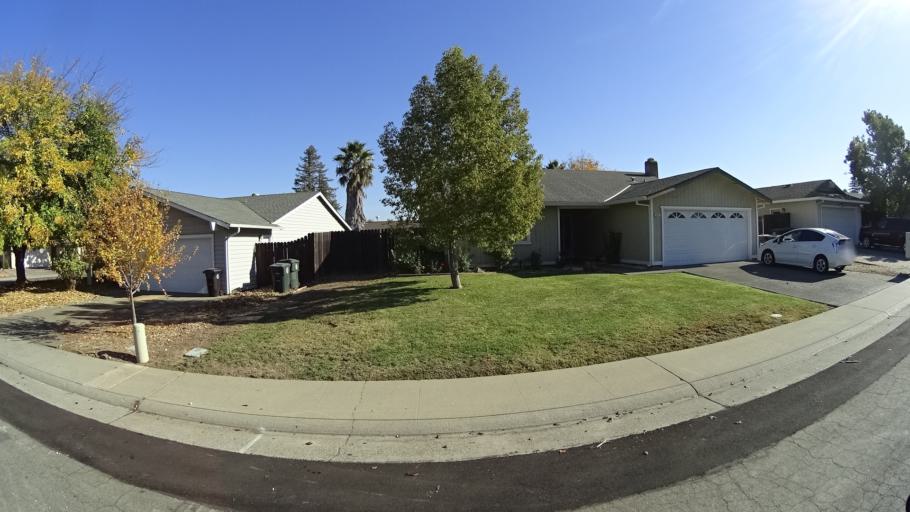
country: US
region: California
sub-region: Sacramento County
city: Antelope
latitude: 38.7140
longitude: -121.3139
